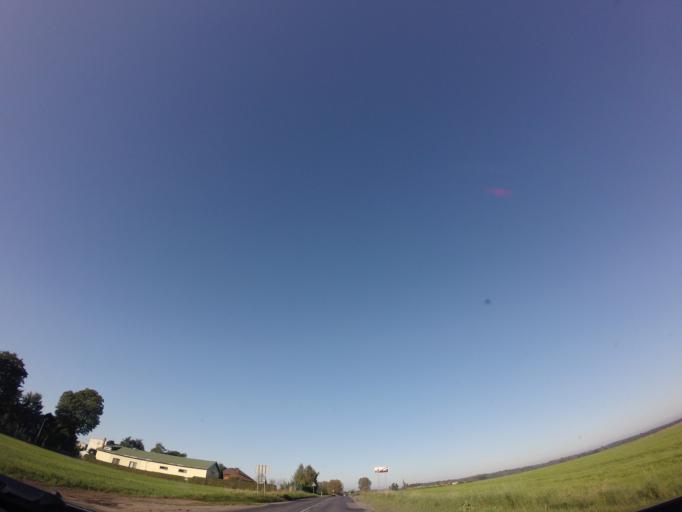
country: PL
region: West Pomeranian Voivodeship
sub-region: Powiat goleniowski
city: Mosty
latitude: 53.5477
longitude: 14.9512
